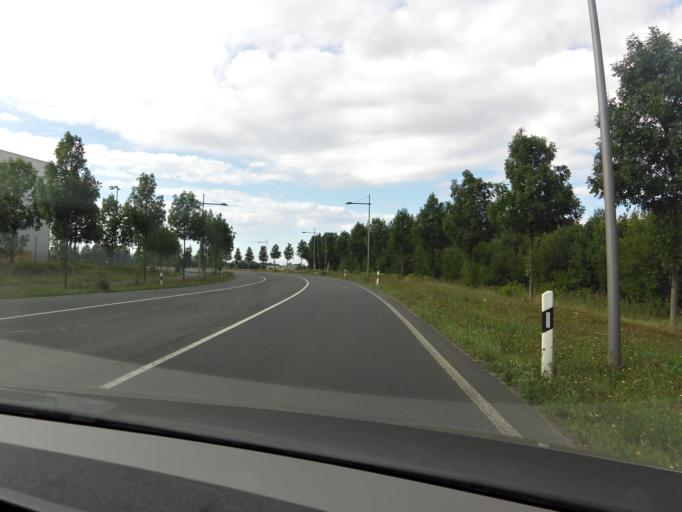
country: DE
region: Saxony
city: Taucha
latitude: 51.4101
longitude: 12.4562
